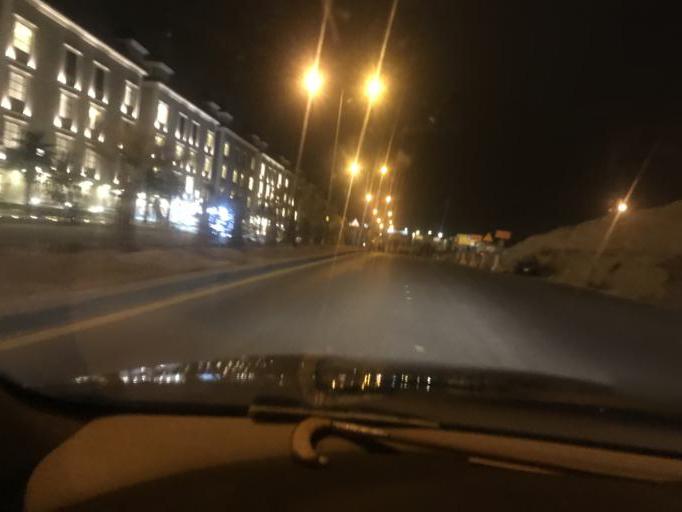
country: SA
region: Ar Riyad
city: Riyadh
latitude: 24.8039
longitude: 46.6828
